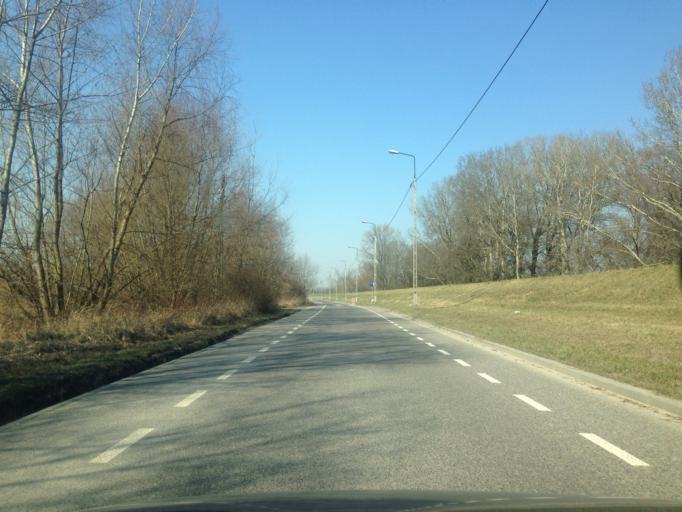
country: PL
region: Masovian Voivodeship
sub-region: Warszawa
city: Wilanow
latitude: 52.1857
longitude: 21.1079
